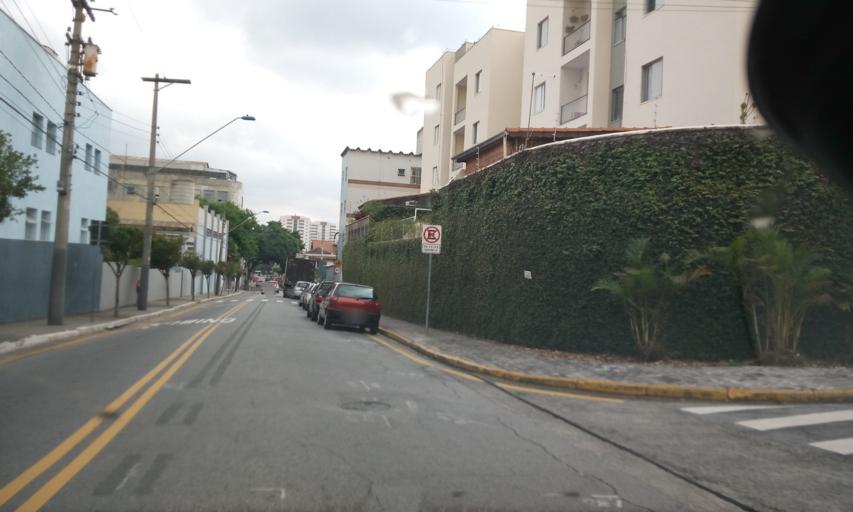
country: BR
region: Sao Paulo
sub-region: Sao Caetano Do Sul
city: Sao Caetano do Sul
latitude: -23.6256
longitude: -46.5715
